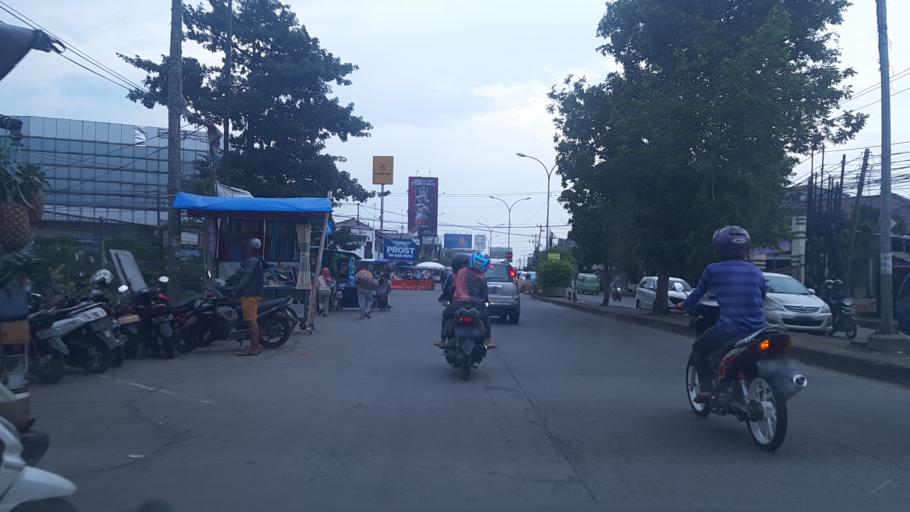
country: ID
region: West Java
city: Cibinong
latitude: -6.4672
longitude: 106.8573
